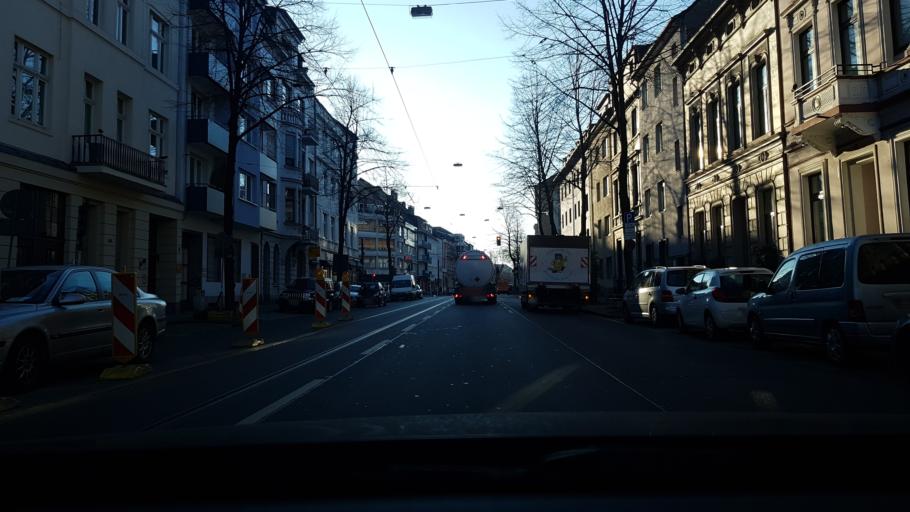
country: DE
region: North Rhine-Westphalia
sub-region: Regierungsbezirk Dusseldorf
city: Dusseldorf
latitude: 51.2357
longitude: 6.7818
